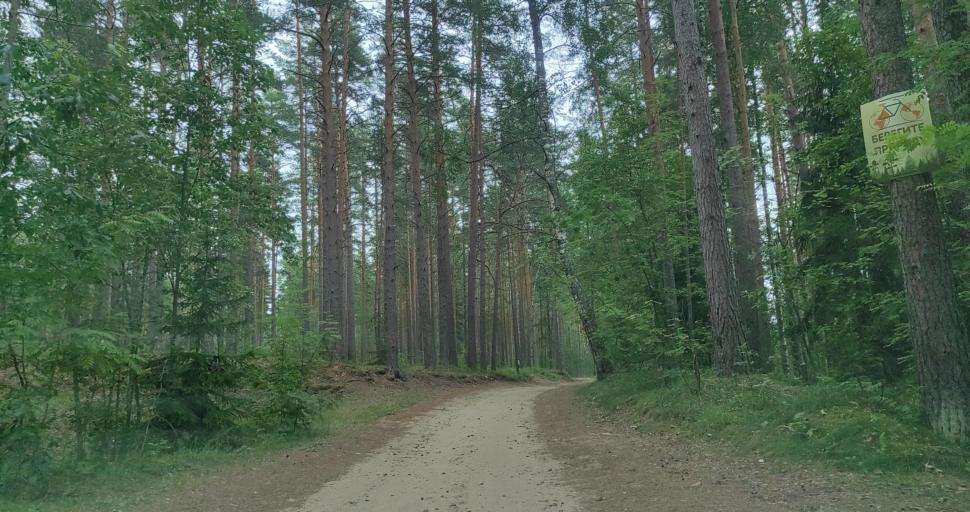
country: RU
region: Leningrad
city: Sapernoye
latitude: 60.6760
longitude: 29.9274
